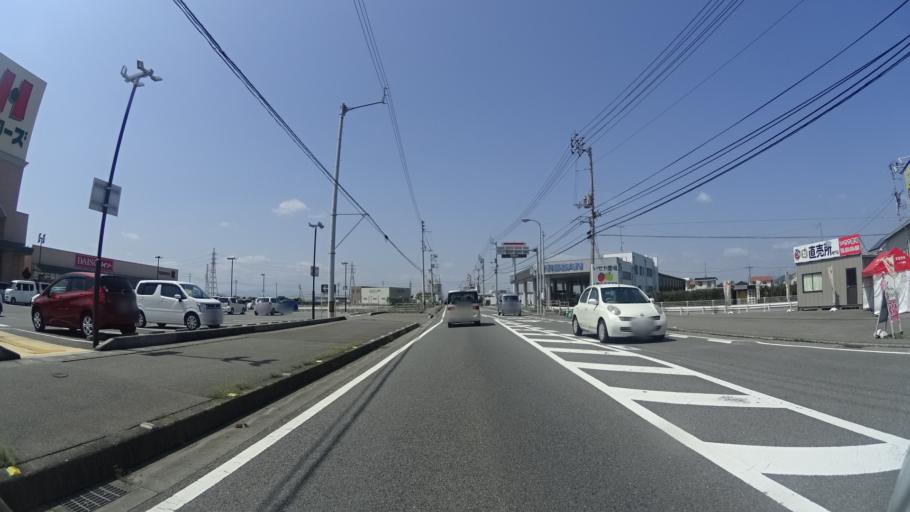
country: JP
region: Tokushima
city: Narutocho-mitsuishi
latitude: 34.1663
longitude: 134.5989
